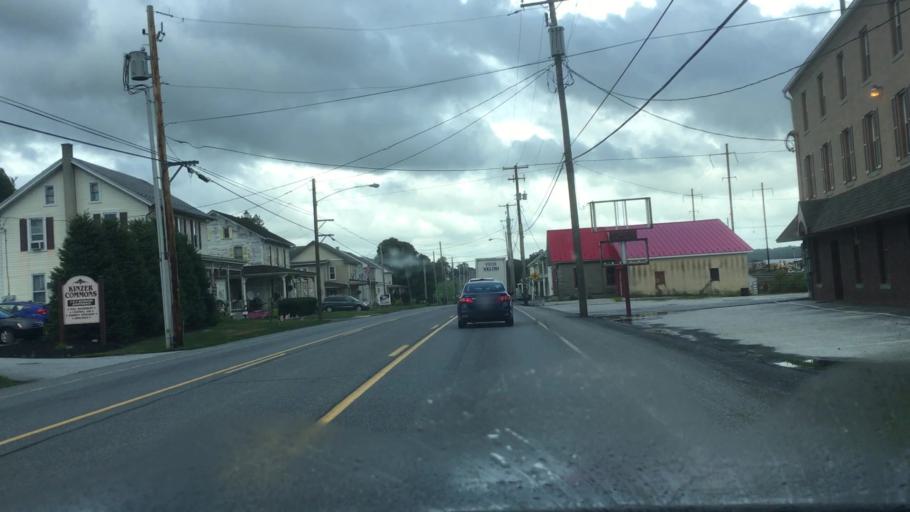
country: US
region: Pennsylvania
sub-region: Lancaster County
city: Gap
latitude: 39.9987
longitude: -76.0637
